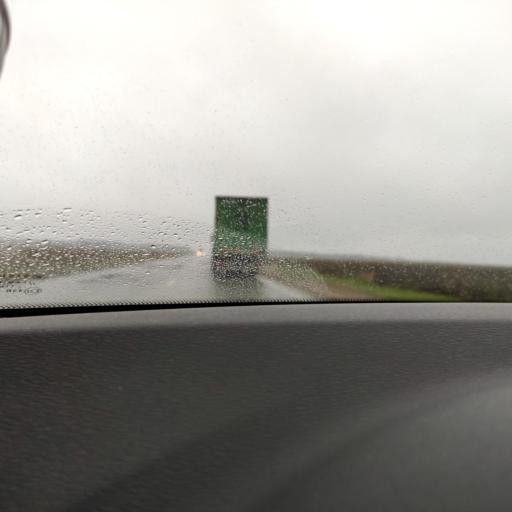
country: RU
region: Samara
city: Yelkhovka
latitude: 53.7155
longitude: 50.2309
